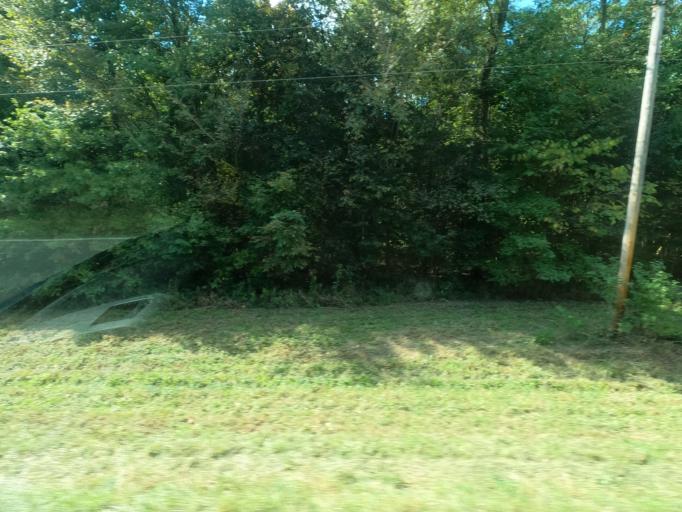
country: US
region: Illinois
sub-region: Massac County
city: Metropolis
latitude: 37.2845
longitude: -88.7577
